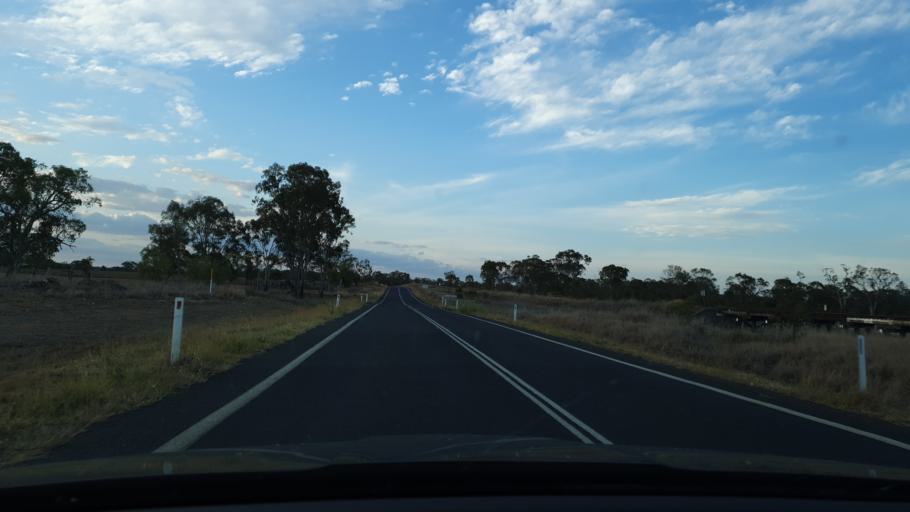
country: AU
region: Queensland
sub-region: Southern Downs
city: Warwick
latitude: -28.1694
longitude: 151.9735
